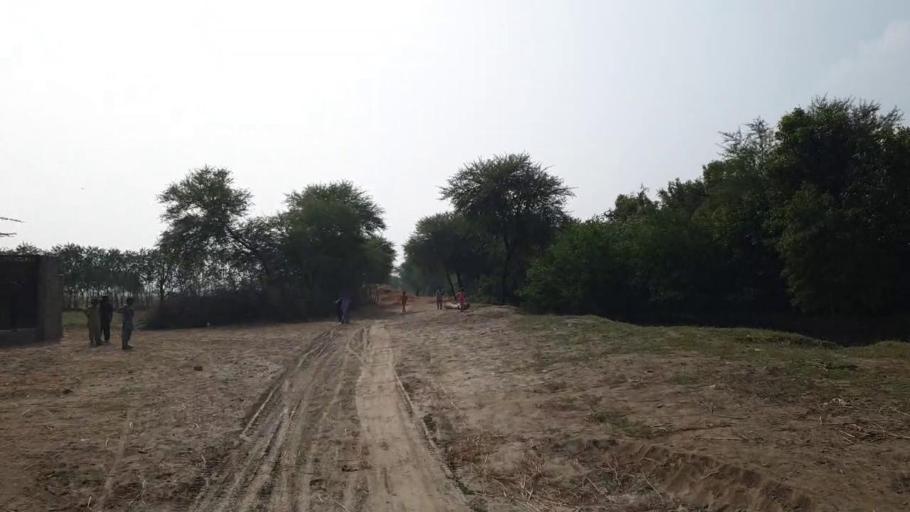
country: PK
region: Sindh
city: Kario
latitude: 24.7719
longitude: 68.5637
